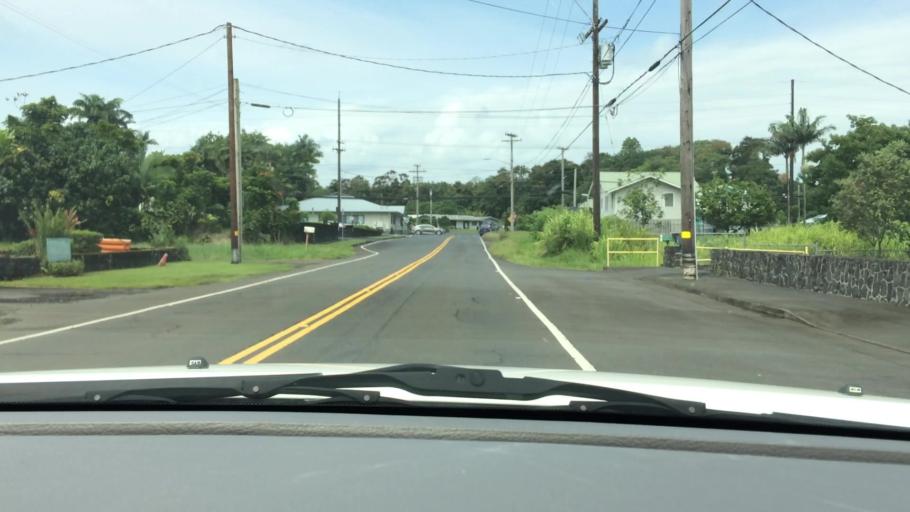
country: US
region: Hawaii
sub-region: Hawaii County
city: Hilo
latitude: 19.7111
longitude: -155.0787
